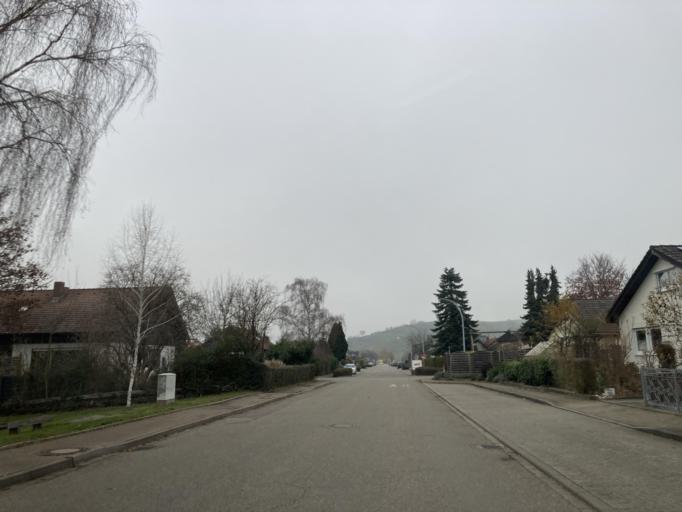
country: DE
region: Baden-Wuerttemberg
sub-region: Freiburg Region
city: Auggen
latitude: 47.7911
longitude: 7.5951
